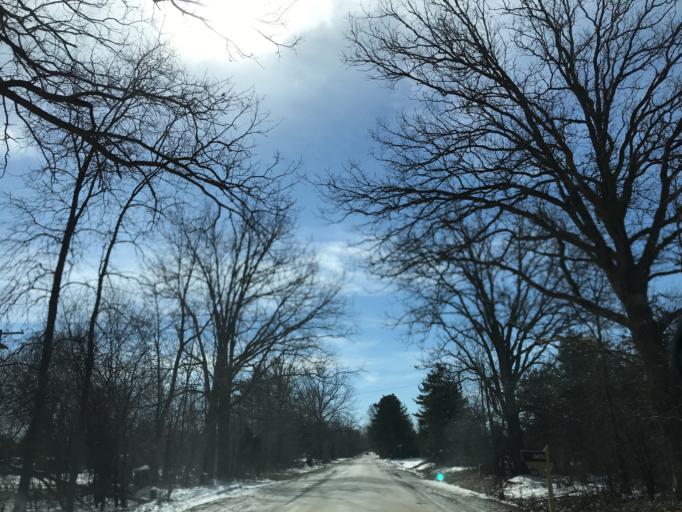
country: US
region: Michigan
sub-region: Livingston County
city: Whitmore Lake
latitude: 42.4236
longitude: -83.7246
